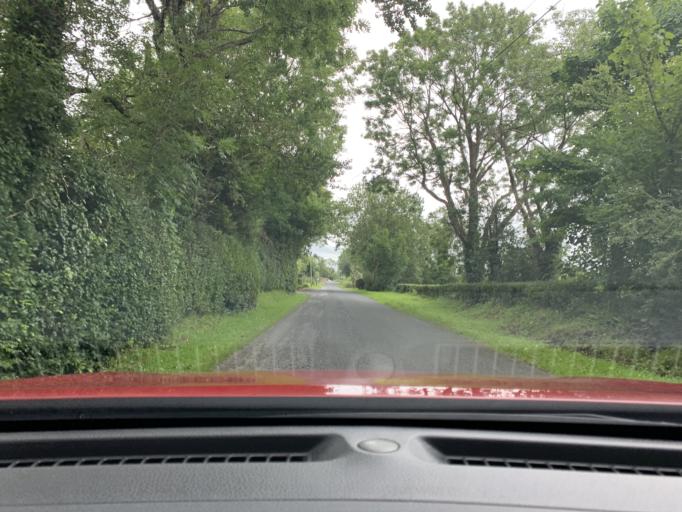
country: IE
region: Connaught
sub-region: Sligo
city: Sligo
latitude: 54.3350
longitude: -8.4709
